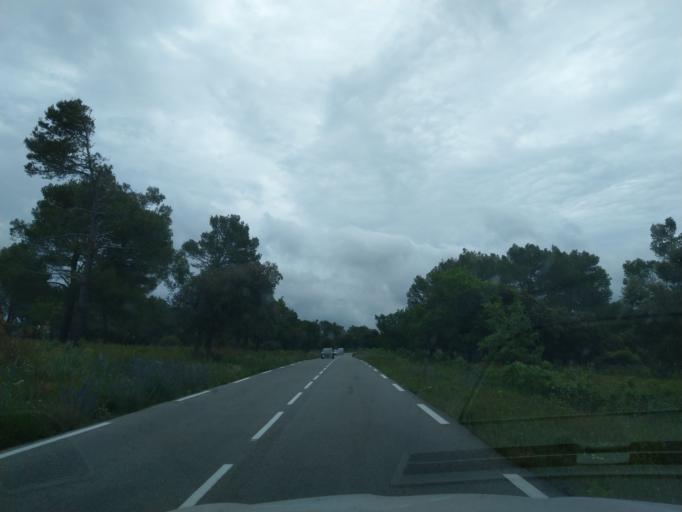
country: FR
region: Provence-Alpes-Cote d'Azur
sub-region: Departement du Var
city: Le Castellet
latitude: 43.2695
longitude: 5.7845
